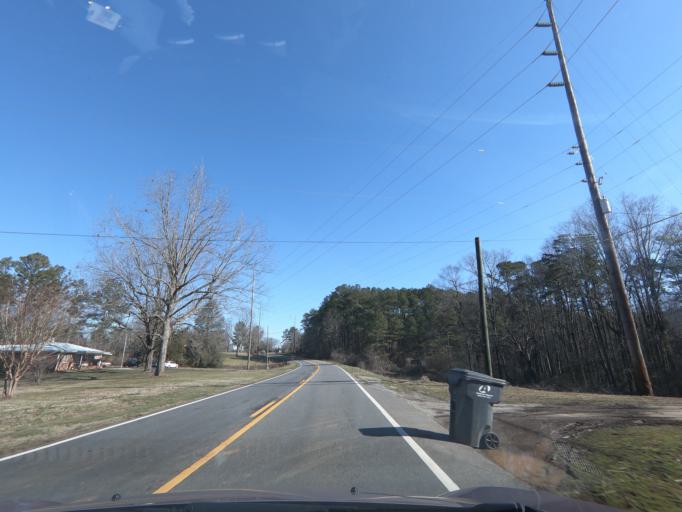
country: US
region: Georgia
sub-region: Forsyth County
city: Cumming
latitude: 34.3126
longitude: -84.1447
